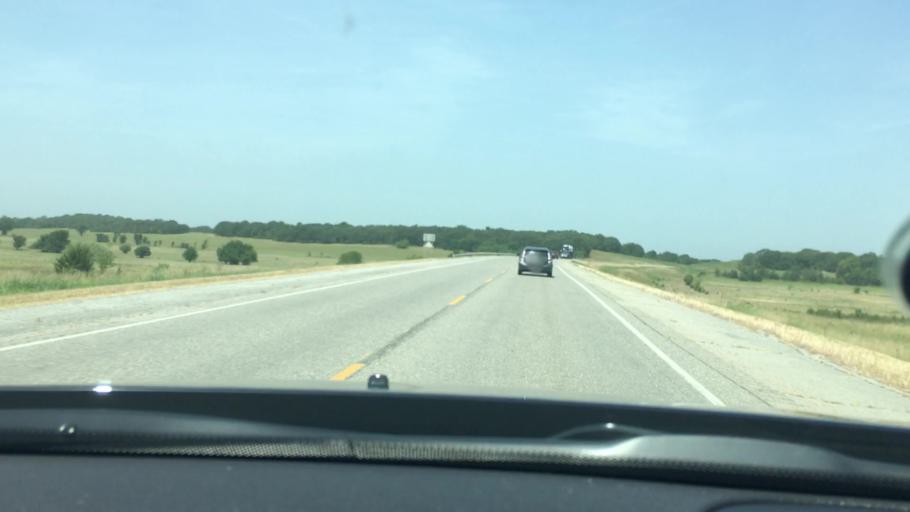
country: US
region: Oklahoma
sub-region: Coal County
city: Coalgate
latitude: 34.6001
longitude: -96.3579
